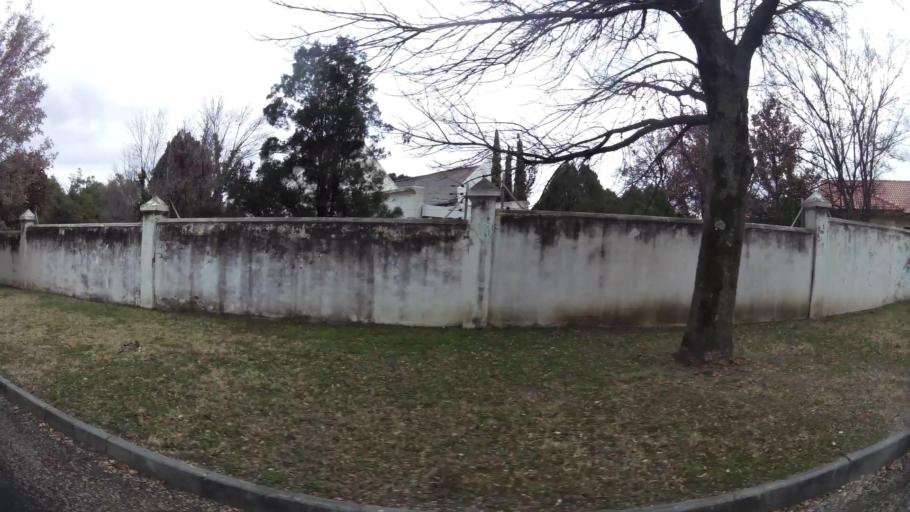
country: ZA
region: Orange Free State
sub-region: Fezile Dabi District Municipality
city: Kroonstad
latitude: -27.6759
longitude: 27.2485
